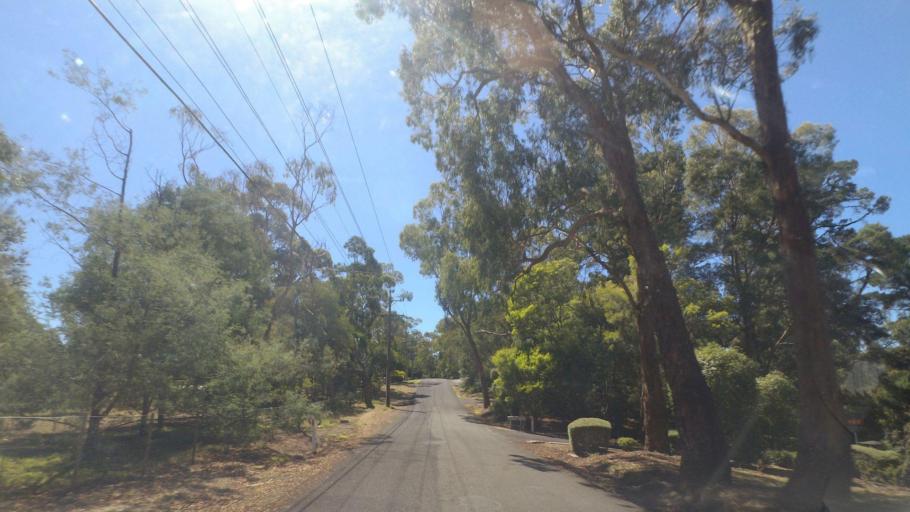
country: AU
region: Victoria
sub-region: Manningham
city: Donvale
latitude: -37.7894
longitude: 145.1910
